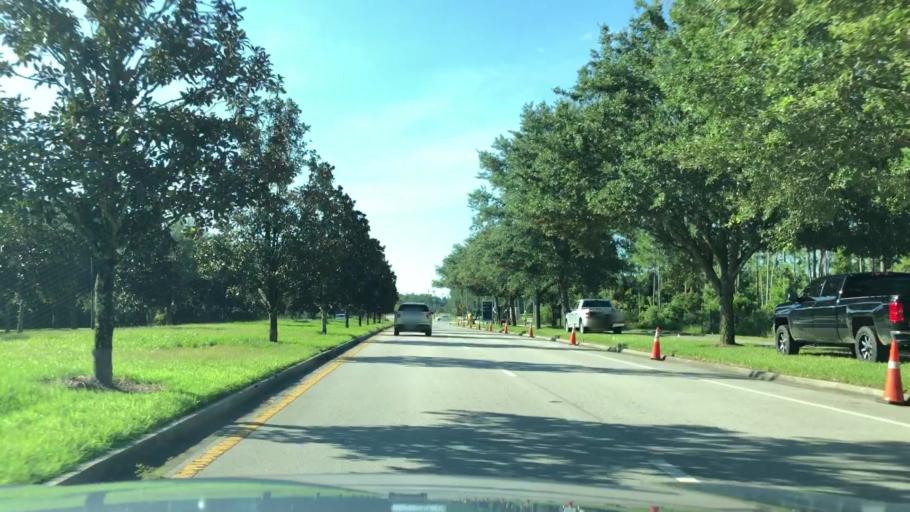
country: US
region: Florida
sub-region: Saint Johns County
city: Palm Valley
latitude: 30.0964
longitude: -81.4093
